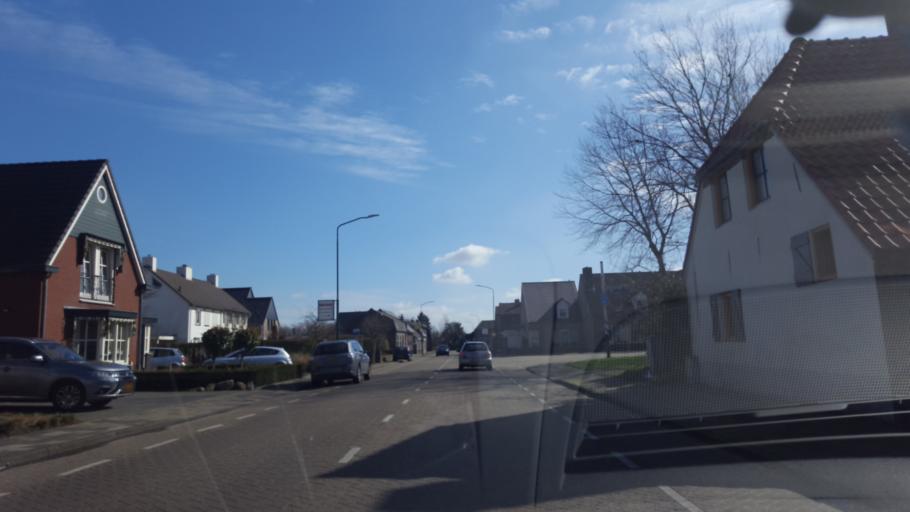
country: NL
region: North Brabant
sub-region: Gemeente Heeze-Leende
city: Heeze
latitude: 51.3738
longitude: 5.5821
